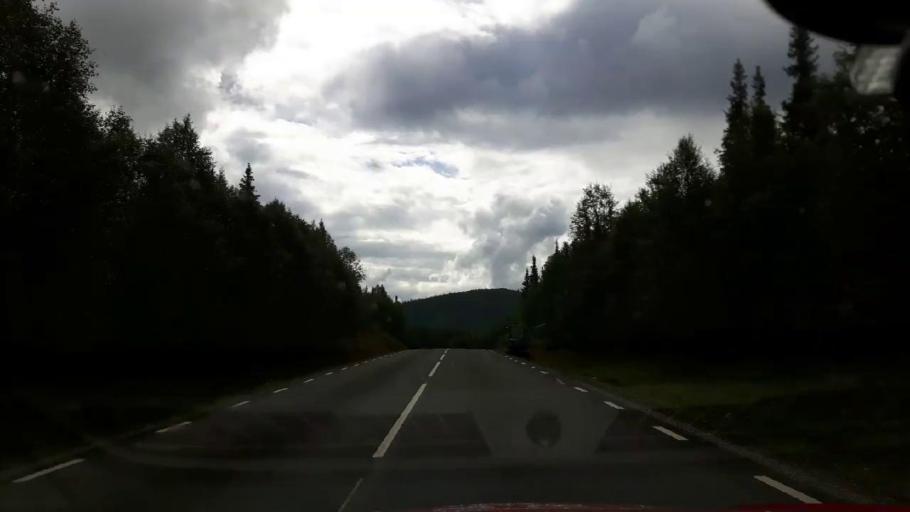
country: NO
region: Nord-Trondelag
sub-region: Royrvik
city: Royrvik
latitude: 64.8981
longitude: 14.1909
